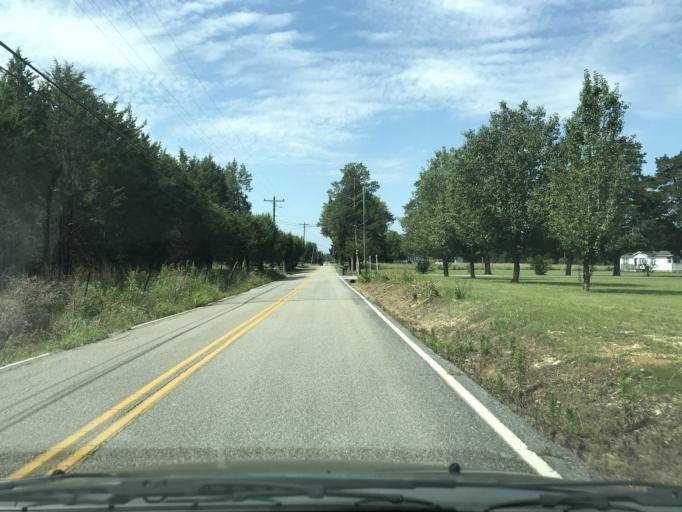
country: US
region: Tennessee
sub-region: Hamilton County
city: Lakesite
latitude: 35.2060
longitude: -85.0240
